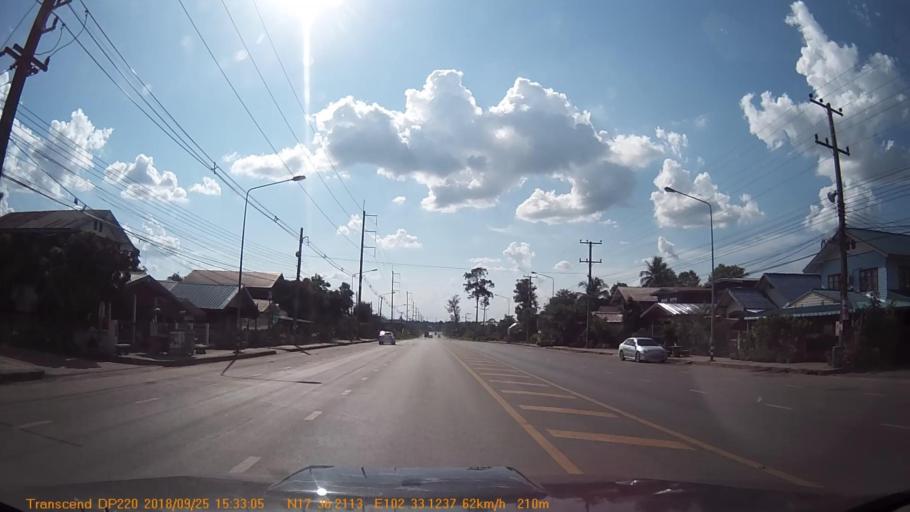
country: TH
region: Changwat Udon Thani
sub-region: Amphoe Ban Phue
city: Ban Phue
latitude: 17.6035
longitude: 102.5516
